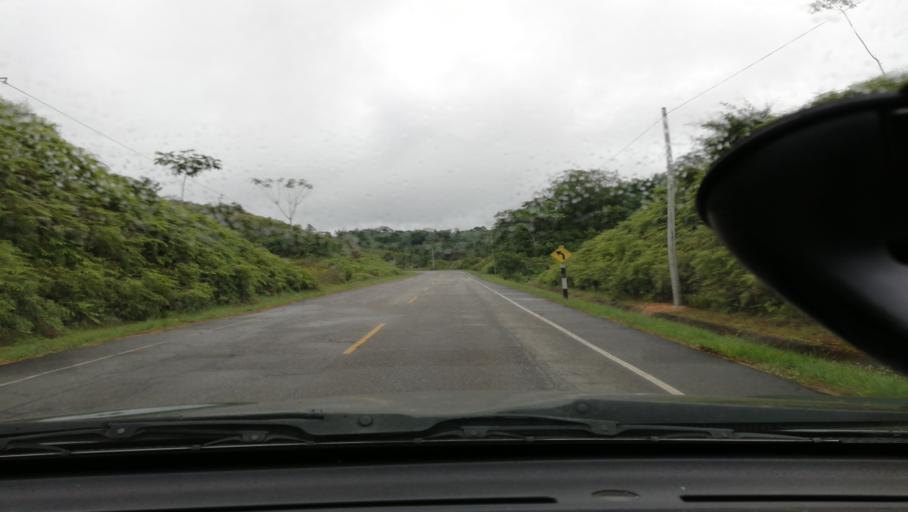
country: PE
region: Loreto
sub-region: Provincia de Loreto
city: Nauta
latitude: -4.4079
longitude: -73.5808
